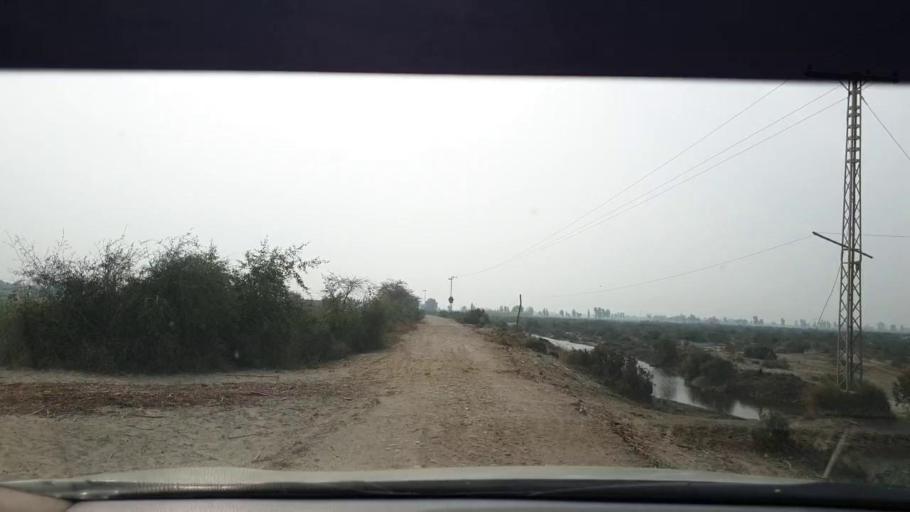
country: PK
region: Sindh
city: Berani
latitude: 25.8382
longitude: 68.8272
